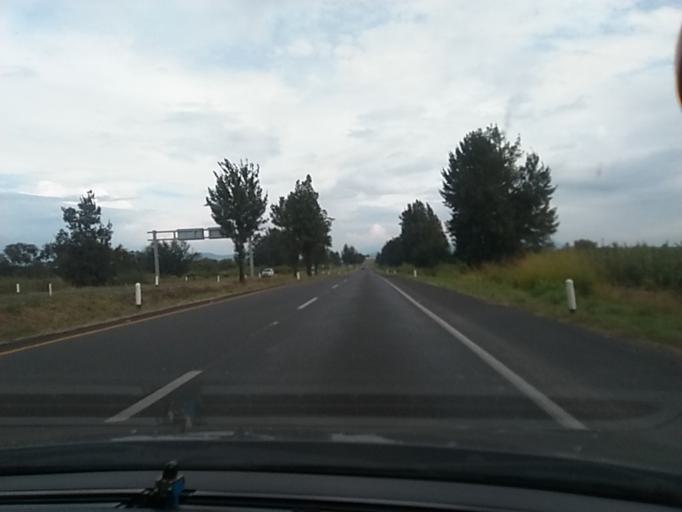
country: MX
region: Michoacan
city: Vistahermosa de Negrete
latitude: 20.2853
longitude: -102.4629
